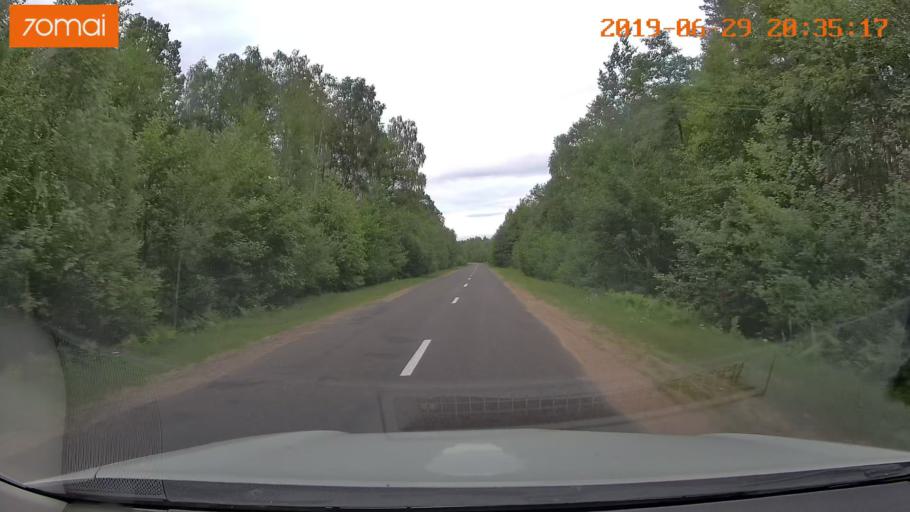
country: BY
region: Brest
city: Hantsavichy
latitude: 52.5156
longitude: 26.3475
